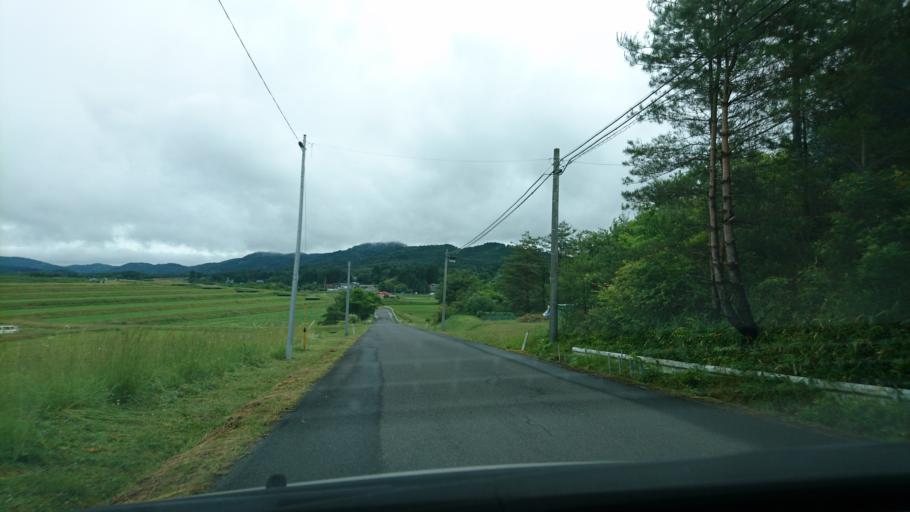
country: JP
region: Iwate
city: Ichinoseki
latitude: 38.9136
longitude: 141.2038
